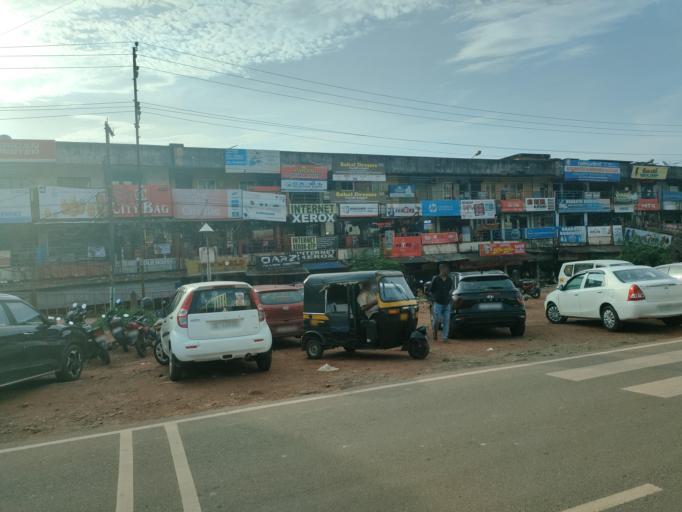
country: IN
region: Kerala
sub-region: Kasaragod District
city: Kasaragod
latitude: 12.5070
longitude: 74.9947
